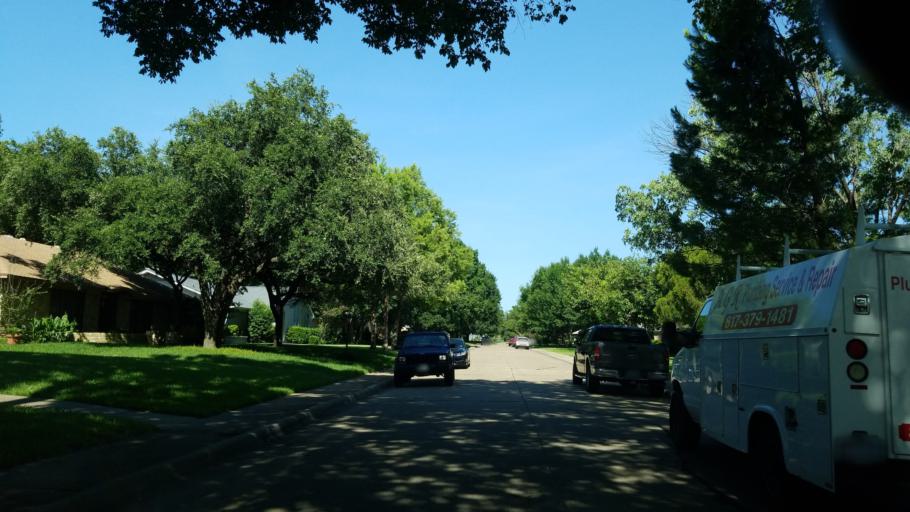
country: US
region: Texas
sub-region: Dallas County
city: Farmers Branch
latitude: 32.9187
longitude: -96.8843
